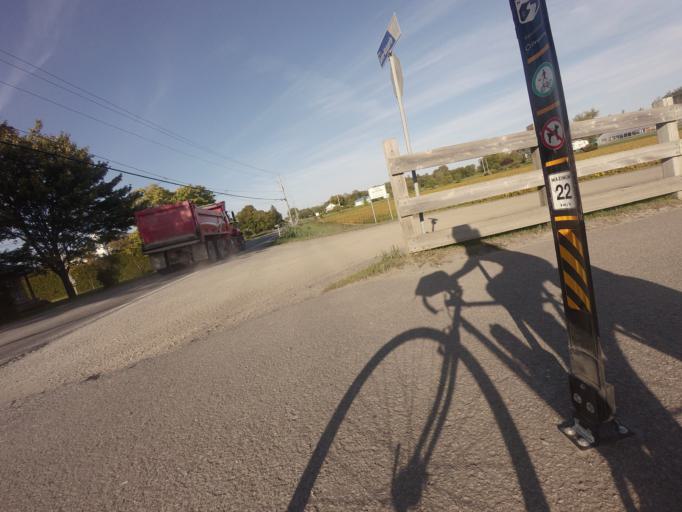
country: CA
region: Quebec
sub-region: Laurentides
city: Saint-Jerome
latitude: 45.7423
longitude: -73.9590
